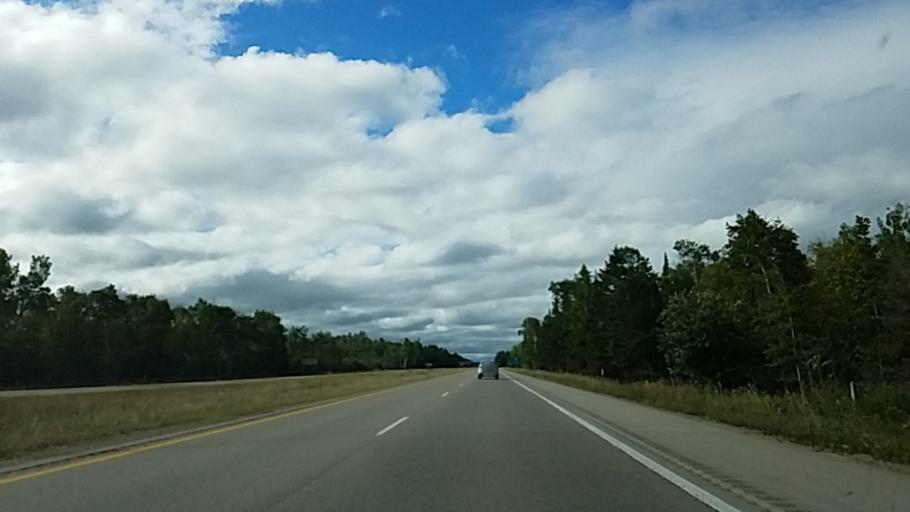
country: US
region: Michigan
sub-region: Mackinac County
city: Saint Ignace
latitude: 45.7419
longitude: -84.7289
